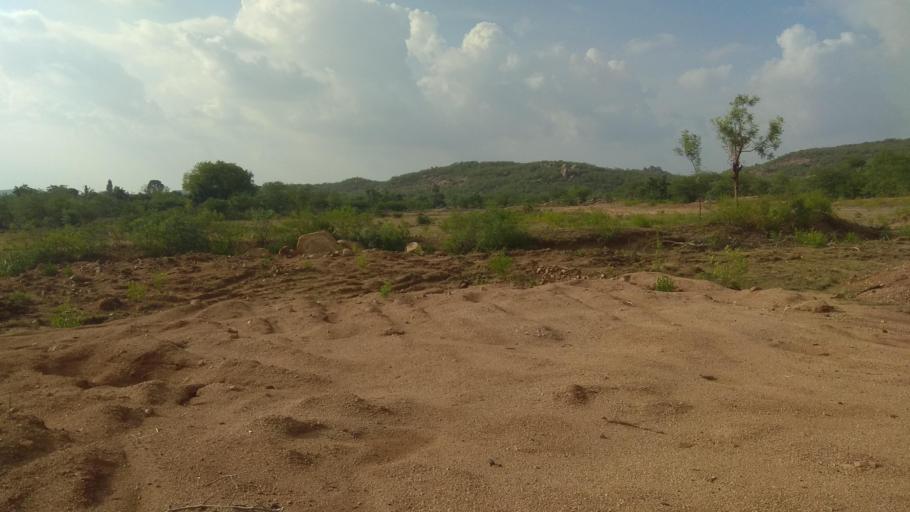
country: IN
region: Telangana
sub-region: Mahbubnagar
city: Farrukhnagar
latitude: 16.8894
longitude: 78.4797
